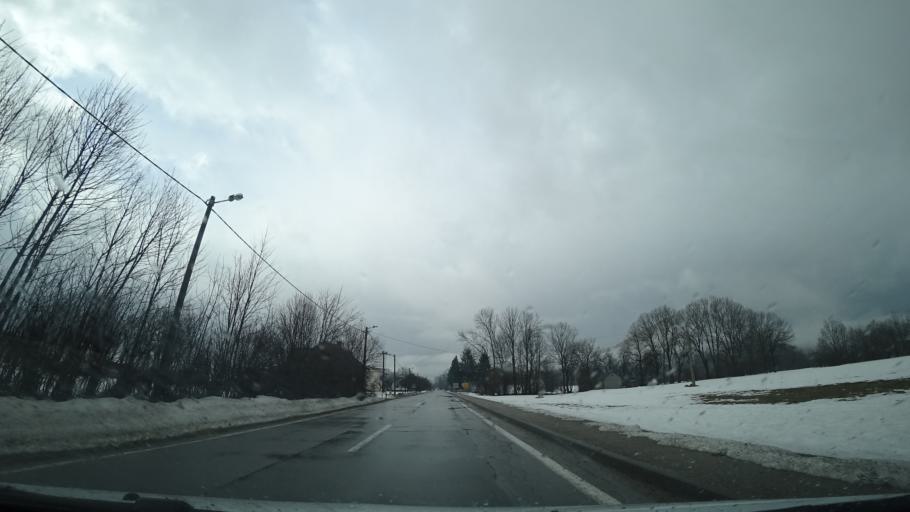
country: HR
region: Licko-Senjska
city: Gospic
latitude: 44.5343
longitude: 15.3442
